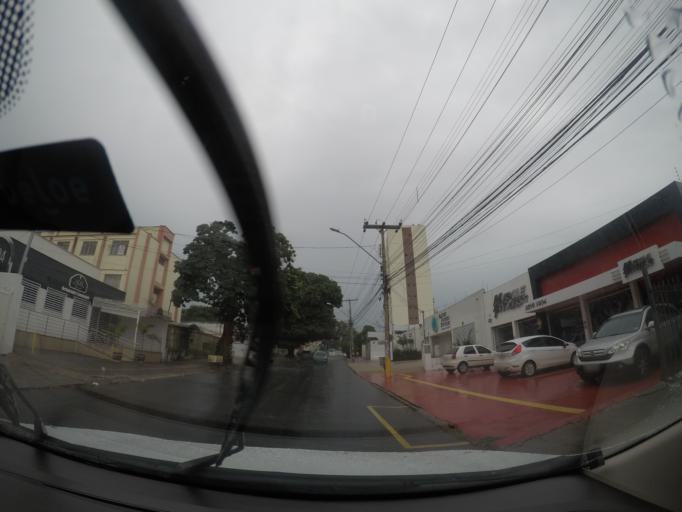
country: BR
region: Goias
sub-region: Goiania
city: Goiania
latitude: -16.6834
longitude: -49.2530
